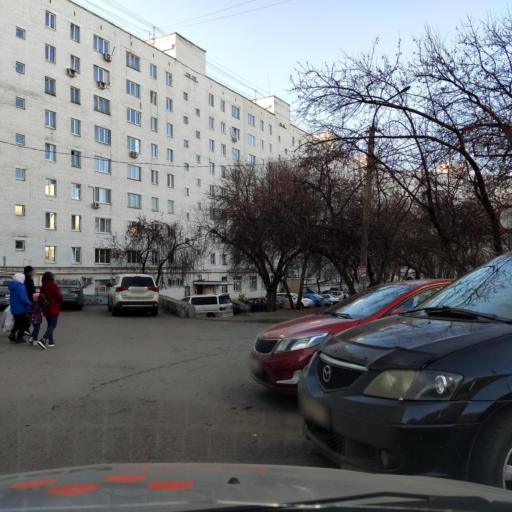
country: RU
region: Bashkortostan
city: Ufa
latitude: 54.7446
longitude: 56.0287
